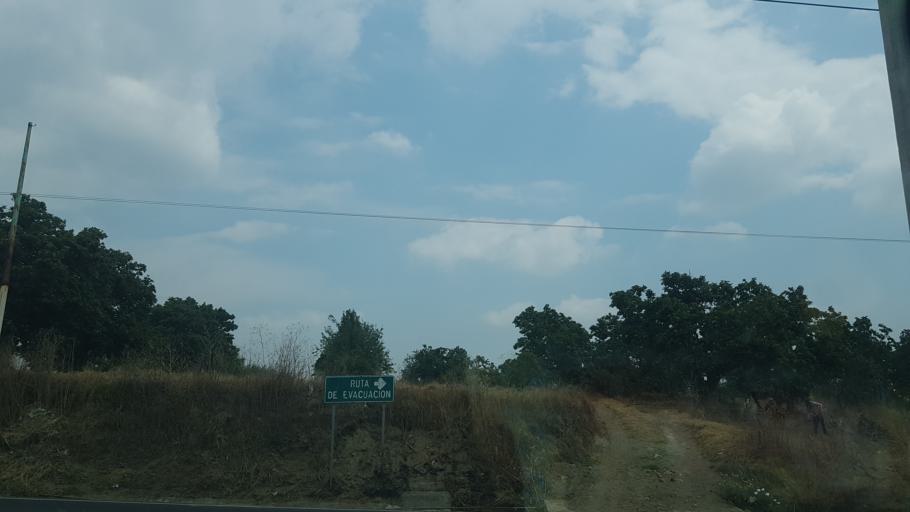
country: MX
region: Puebla
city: Domingo Arenas
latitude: 19.1422
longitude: -98.4776
